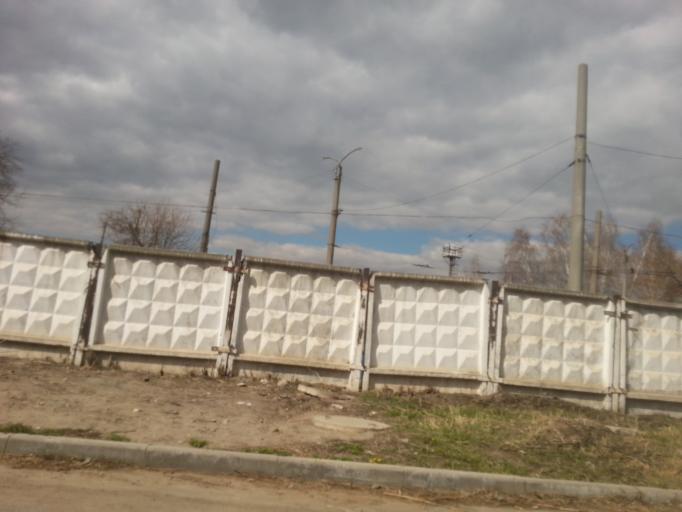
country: RU
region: Altai Krai
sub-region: Gorod Barnaulskiy
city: Barnaul
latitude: 53.3834
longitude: 83.7105
